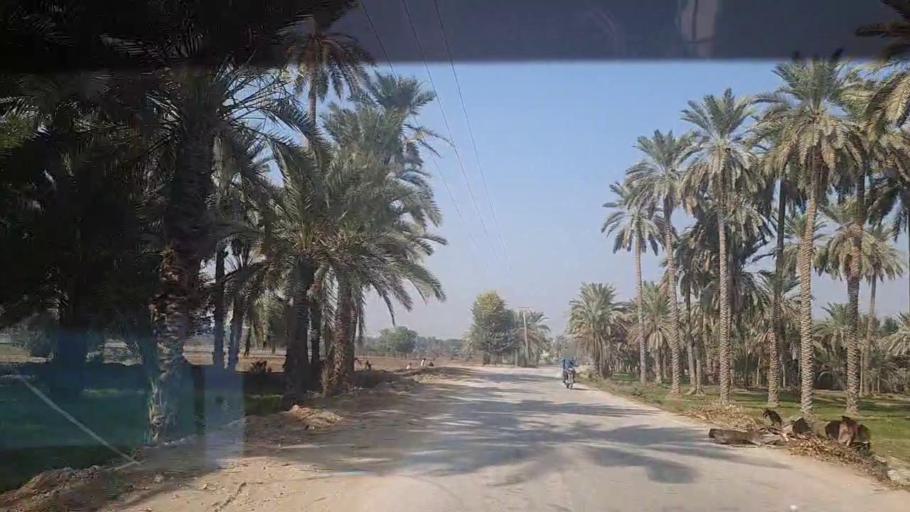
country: PK
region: Sindh
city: Kot Diji
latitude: 27.3807
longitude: 68.6899
